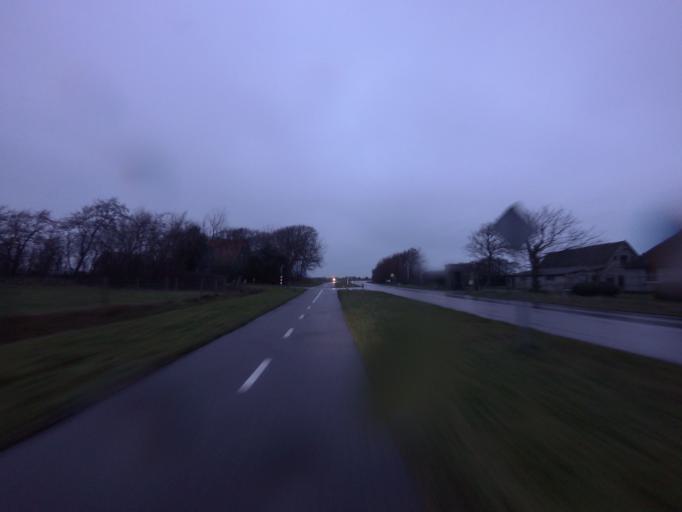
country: NL
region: North Holland
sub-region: Gemeente Texel
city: Den Burg
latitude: 53.0642
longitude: 4.8027
